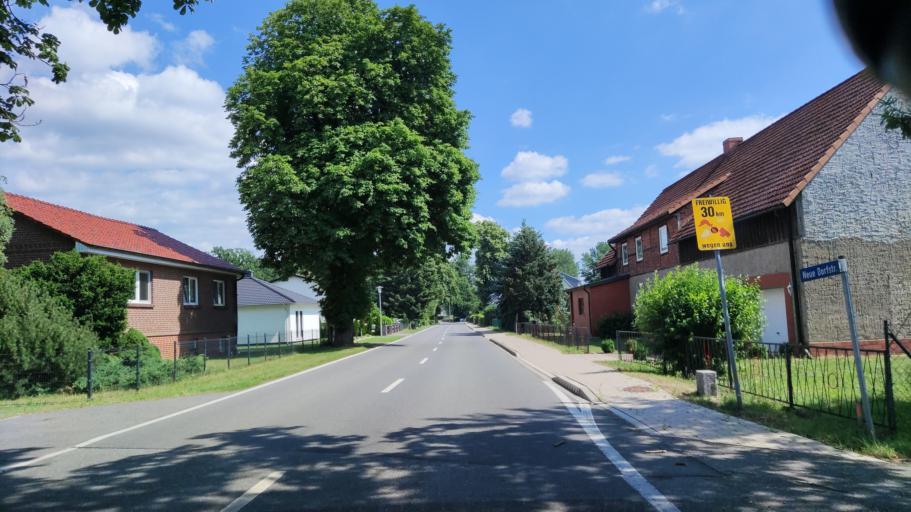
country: DE
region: Mecklenburg-Vorpommern
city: Lubtheen
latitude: 53.2626
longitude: 11.1038
